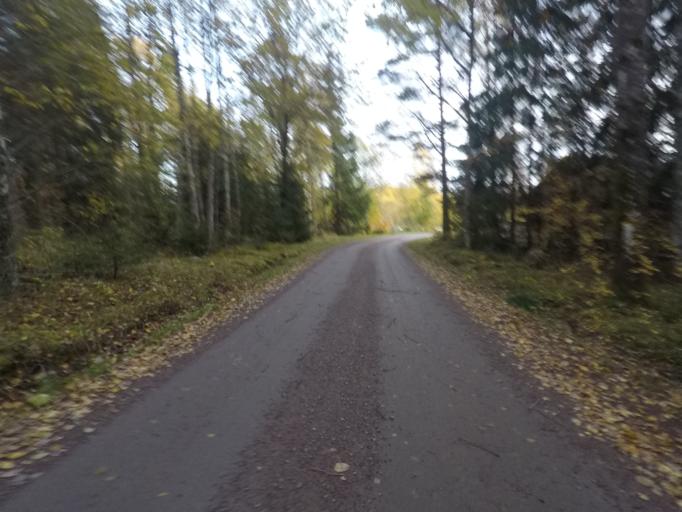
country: SE
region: OErebro
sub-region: Karlskoga Kommun
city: Karlskoga
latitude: 59.2957
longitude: 14.4948
